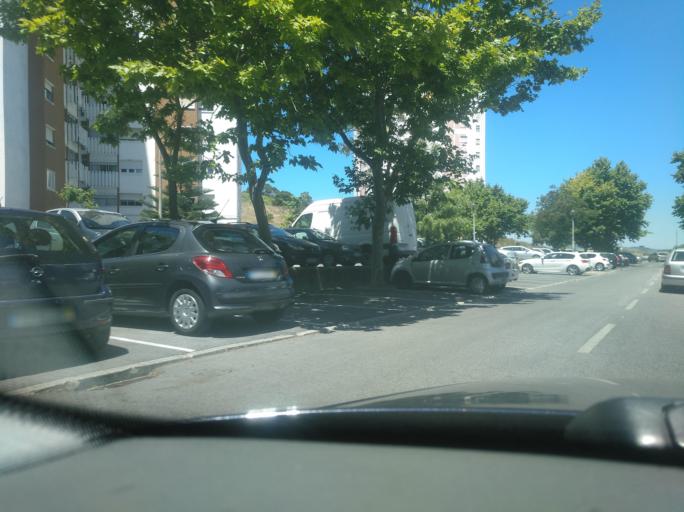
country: PT
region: Lisbon
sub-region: Odivelas
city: Ramada
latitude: 38.8133
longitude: -9.1804
